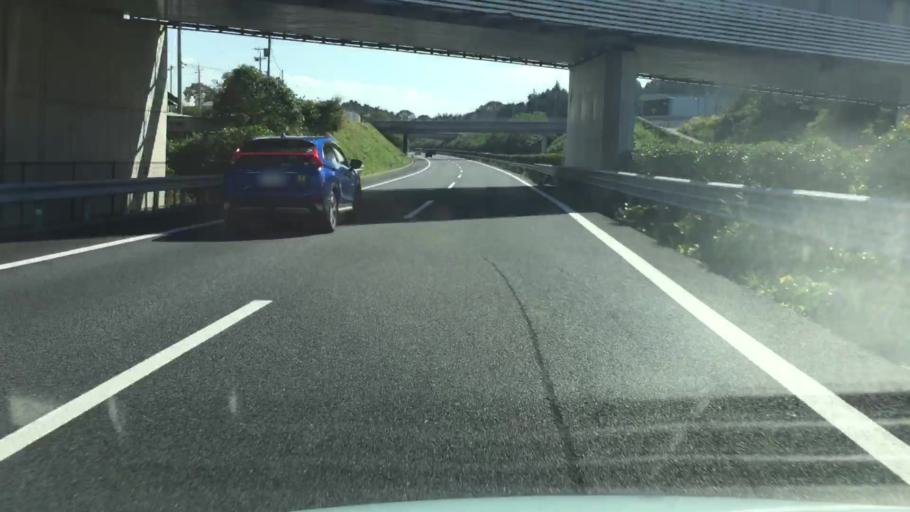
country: JP
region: Ibaraki
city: Tomobe
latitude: 36.3166
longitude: 140.3140
